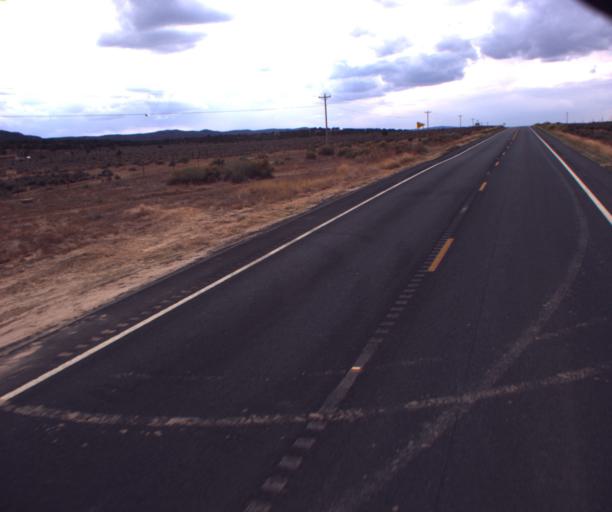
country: US
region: Arizona
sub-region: Navajo County
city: Kayenta
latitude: 36.5215
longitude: -110.5851
